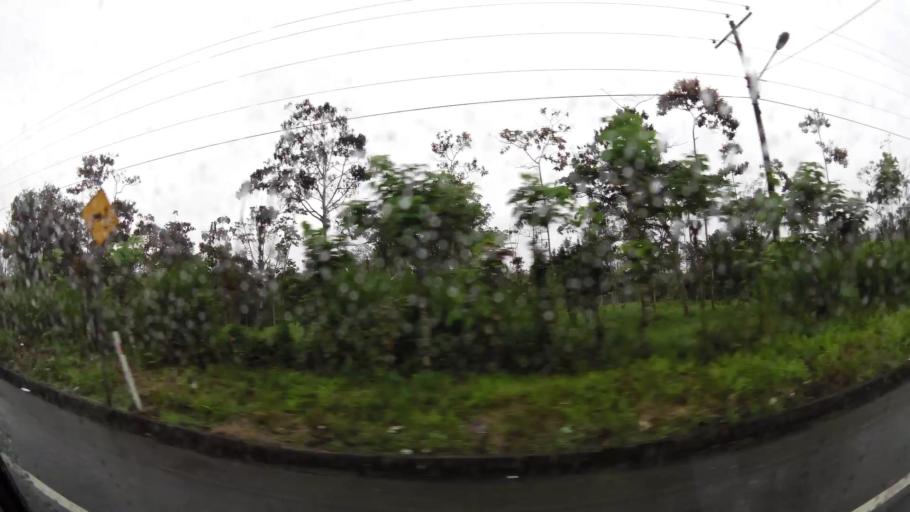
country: EC
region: Santo Domingo de los Tsachilas
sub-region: Canton Santo Domingo de los Colorados
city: Santo Domingo de los Colorados
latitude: -0.2190
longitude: -79.1206
